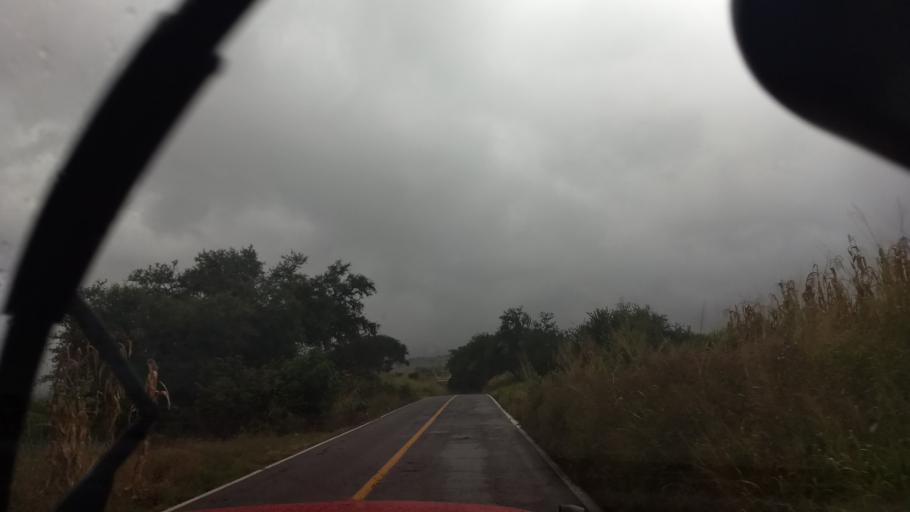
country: MX
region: Jalisco
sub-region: Tonila
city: San Marcos
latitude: 19.4392
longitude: -103.4913
